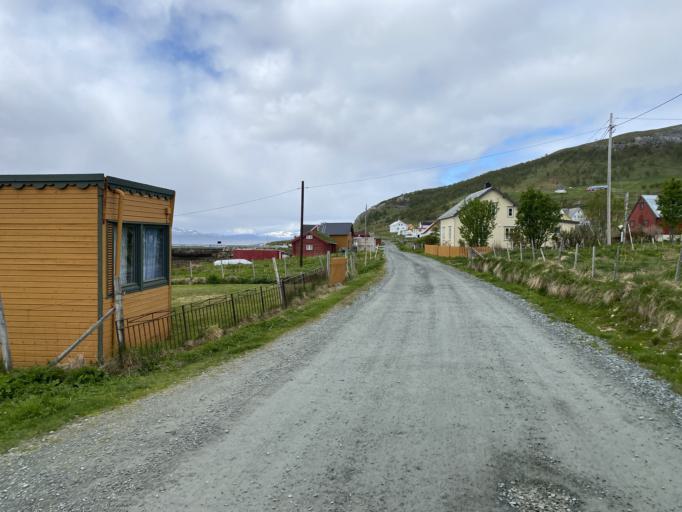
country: NO
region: Troms
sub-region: Karlsoy
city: Hansnes
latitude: 70.0015
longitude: 19.8937
